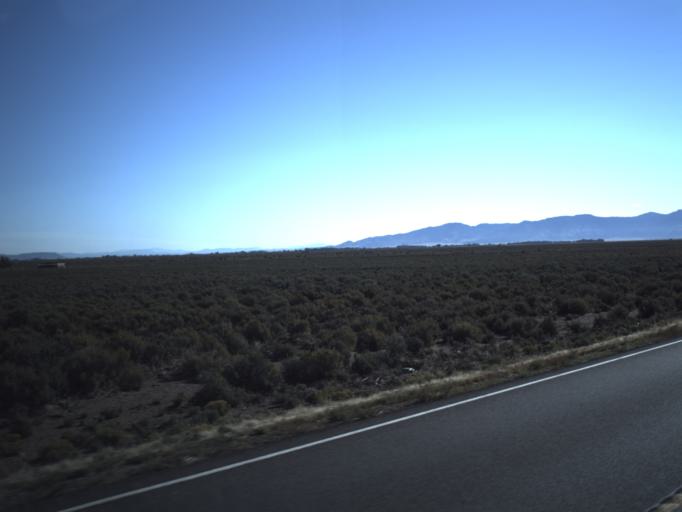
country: US
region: Utah
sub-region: Washington County
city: Enterprise
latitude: 37.7322
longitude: -113.7194
